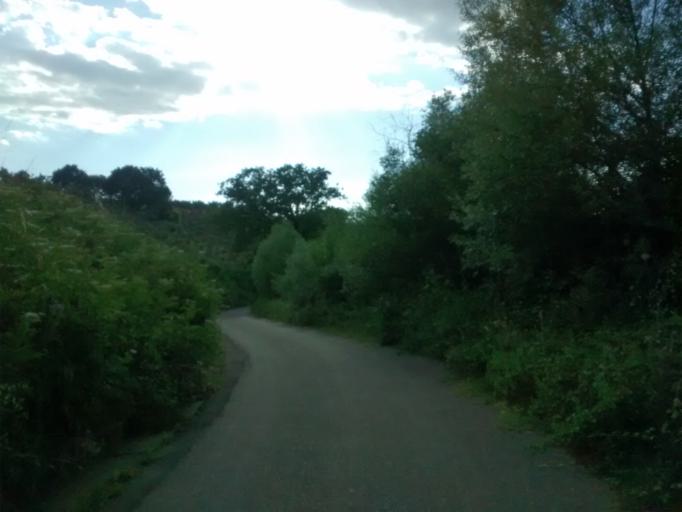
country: IT
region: Calabria
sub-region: Provincia di Catanzaro
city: Cortale
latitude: 38.8824
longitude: 16.4119
